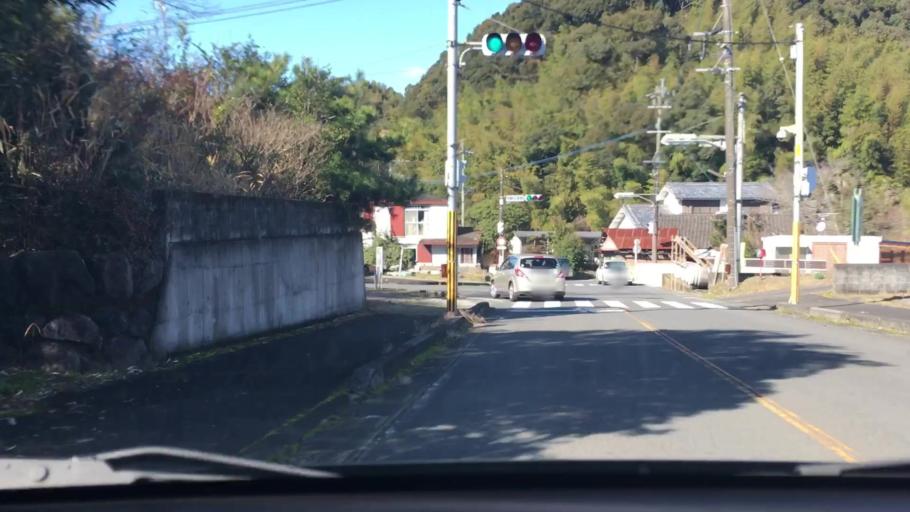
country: JP
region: Kagoshima
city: Satsumasendai
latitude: 31.7787
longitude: 130.4001
